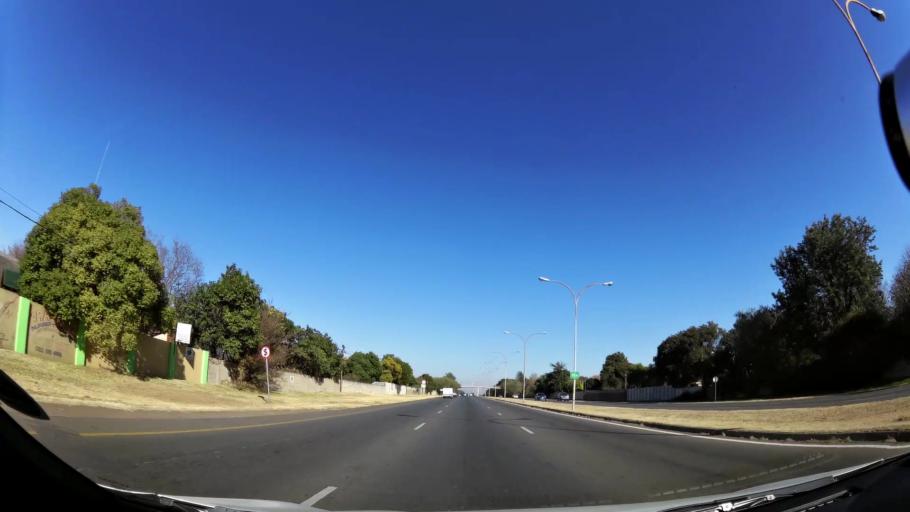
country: ZA
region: Gauteng
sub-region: Ekurhuleni Metropolitan Municipality
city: Germiston
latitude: -26.3087
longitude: 28.1042
